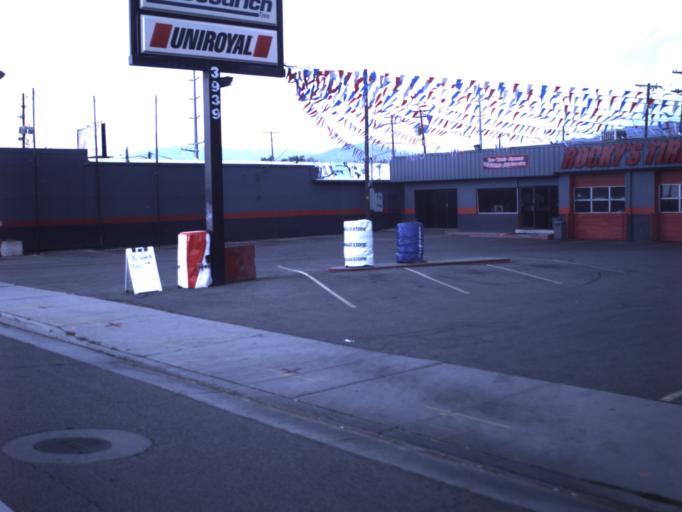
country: US
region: Utah
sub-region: Salt Lake County
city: Centerfield
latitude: 40.6860
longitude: -111.8882
